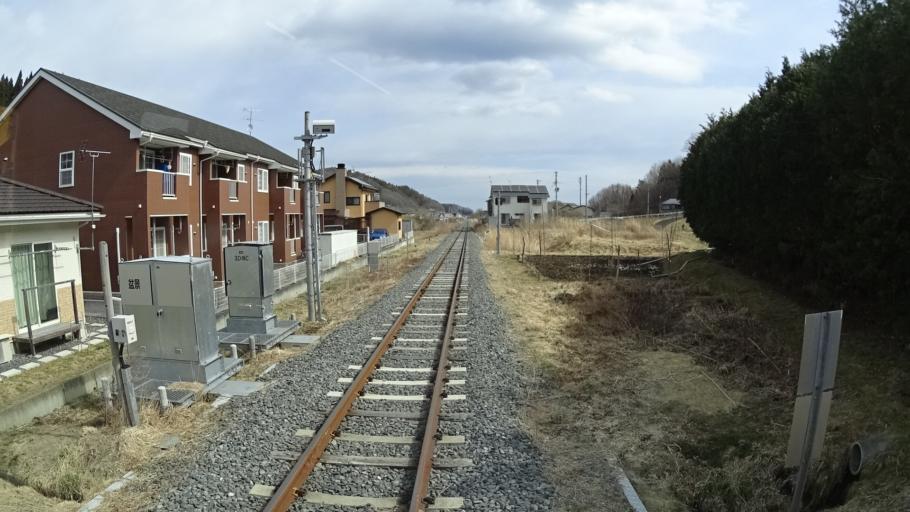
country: JP
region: Iwate
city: Miyako
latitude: 39.6160
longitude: 141.9412
